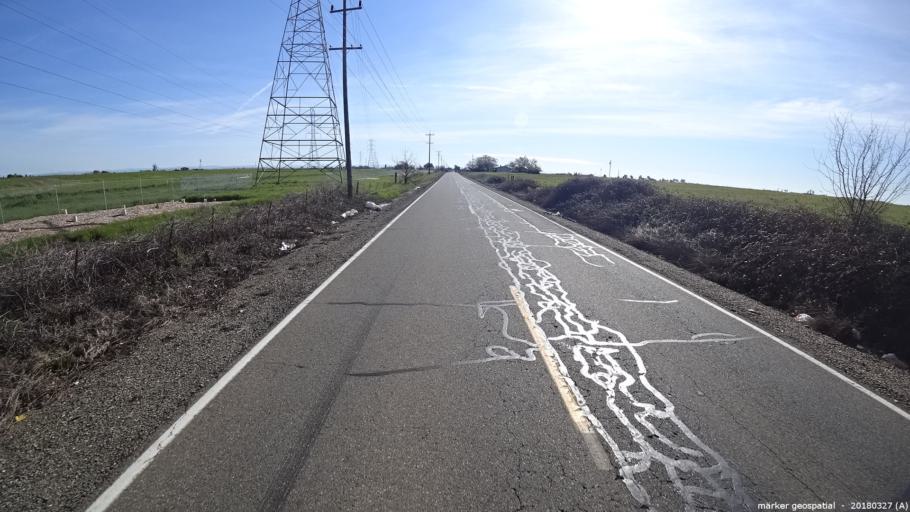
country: US
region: California
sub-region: Sacramento County
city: Vineyard
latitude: 38.5109
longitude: -121.3202
